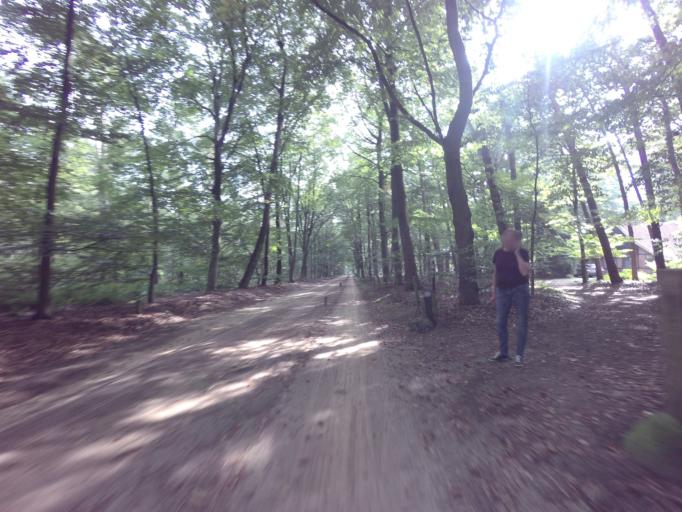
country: DE
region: Lower Saxony
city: Getelo
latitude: 52.4361
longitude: 6.8765
